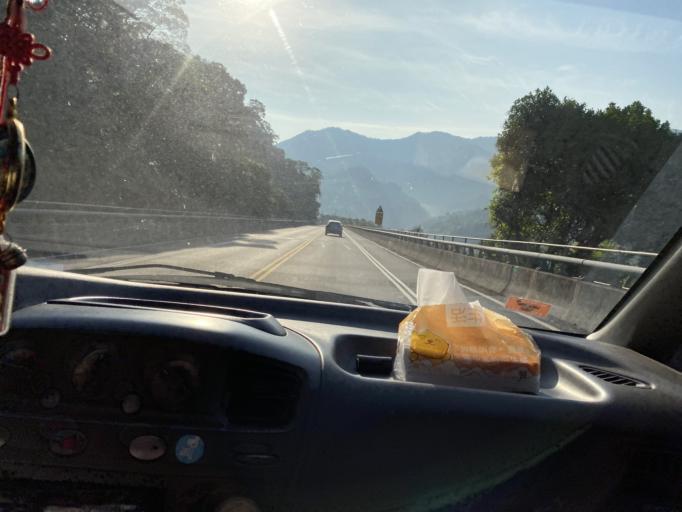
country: TW
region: Taiwan
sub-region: Keelung
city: Keelung
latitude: 25.0174
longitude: 121.7975
